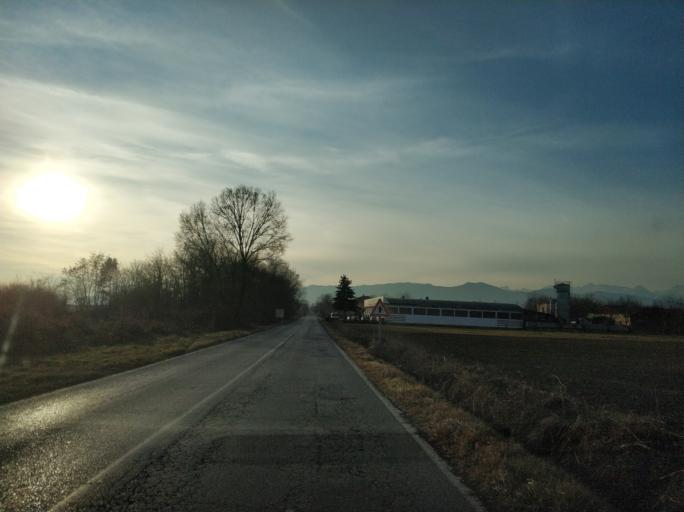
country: IT
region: Piedmont
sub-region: Provincia di Torino
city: San Francesco al Campo
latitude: 45.2204
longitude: 7.6499
